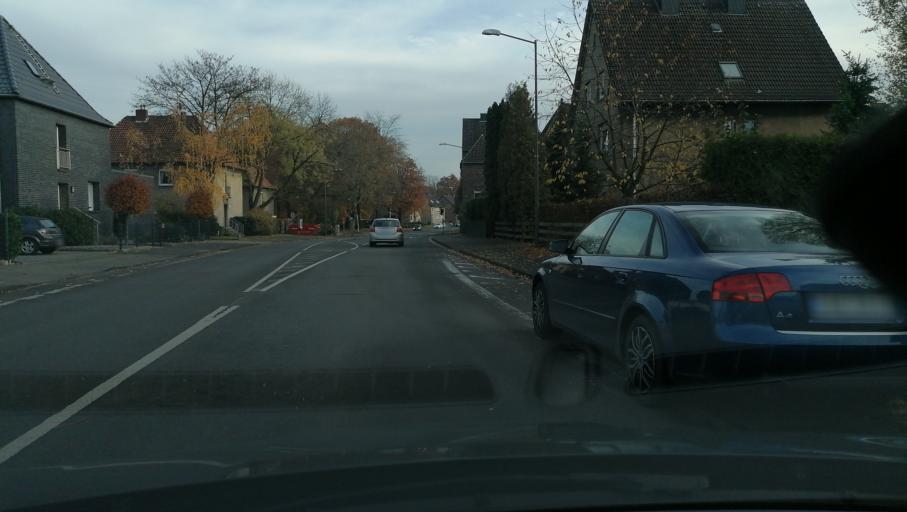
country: DE
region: North Rhine-Westphalia
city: Castrop-Rauxel
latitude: 51.5881
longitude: 7.3185
